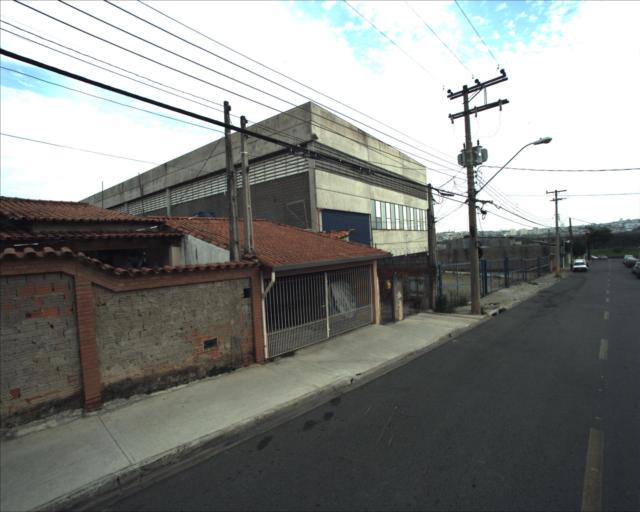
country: BR
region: Sao Paulo
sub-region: Sorocaba
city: Sorocaba
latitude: -23.4621
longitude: -47.4427
